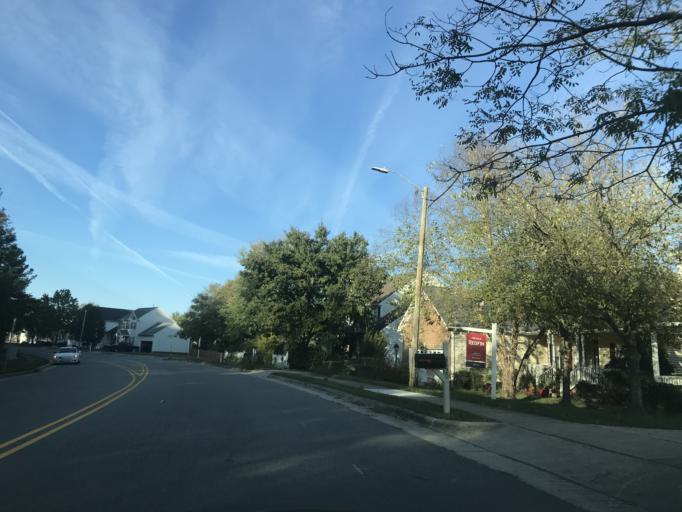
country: US
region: North Carolina
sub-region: Wake County
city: Wake Forest
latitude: 35.8930
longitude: -78.5491
